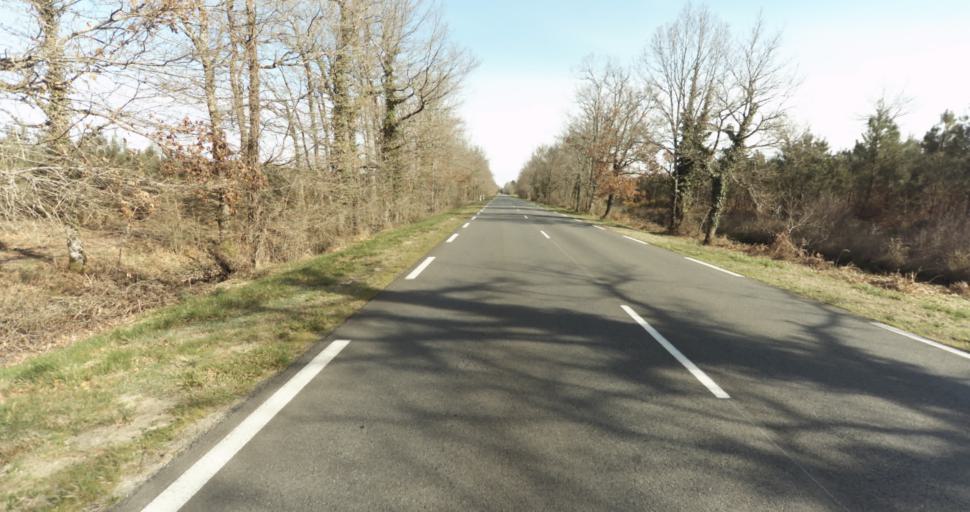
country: FR
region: Aquitaine
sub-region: Departement des Landes
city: Roquefort
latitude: 44.0933
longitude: -0.3086
